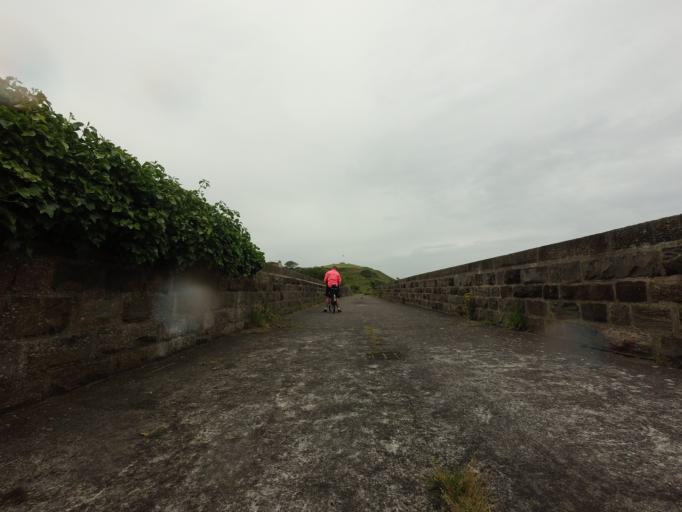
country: GB
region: Scotland
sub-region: Moray
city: Cullen
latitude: 57.6913
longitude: -2.8222
